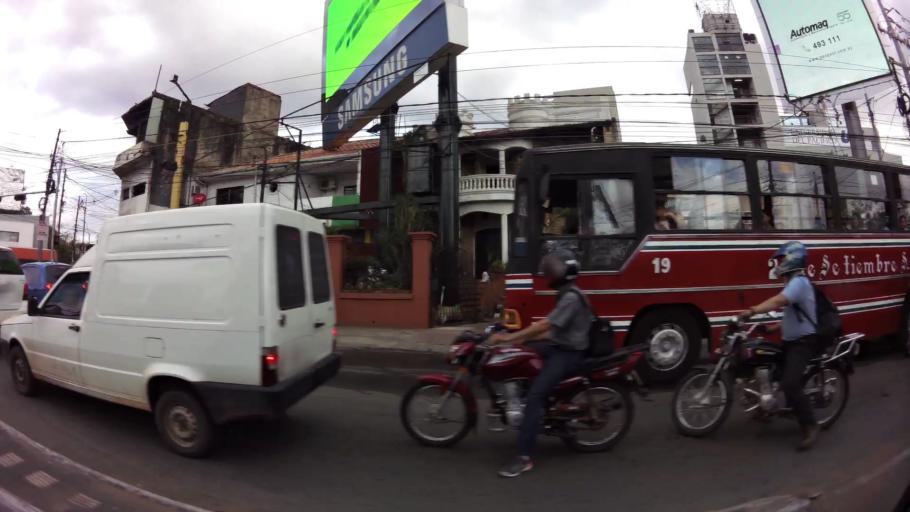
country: PY
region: Asuncion
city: Asuncion
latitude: -25.2865
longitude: -57.5721
